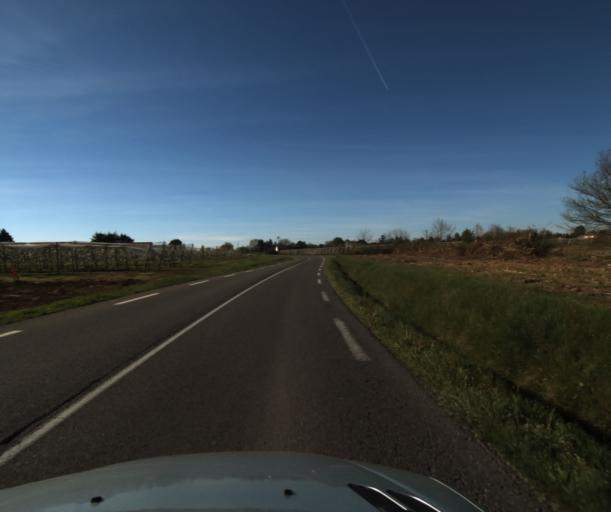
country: FR
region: Midi-Pyrenees
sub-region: Departement du Tarn-et-Garonne
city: Montbeton
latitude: 44.0359
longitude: 1.3113
